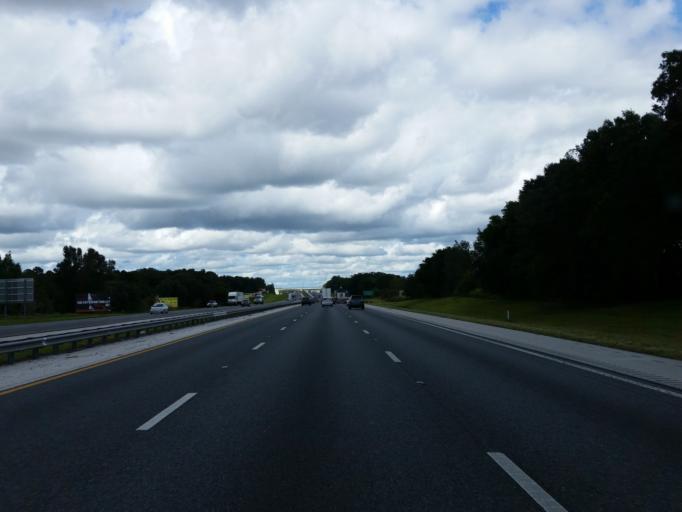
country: US
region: Florida
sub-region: Marion County
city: Ocala
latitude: 29.1317
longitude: -82.1846
